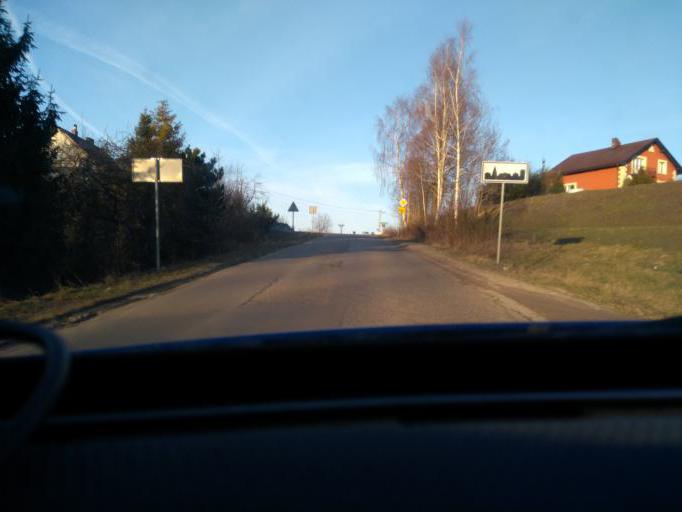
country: PL
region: Pomeranian Voivodeship
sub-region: Powiat kartuski
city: Przodkowo
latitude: 54.4134
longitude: 18.3124
